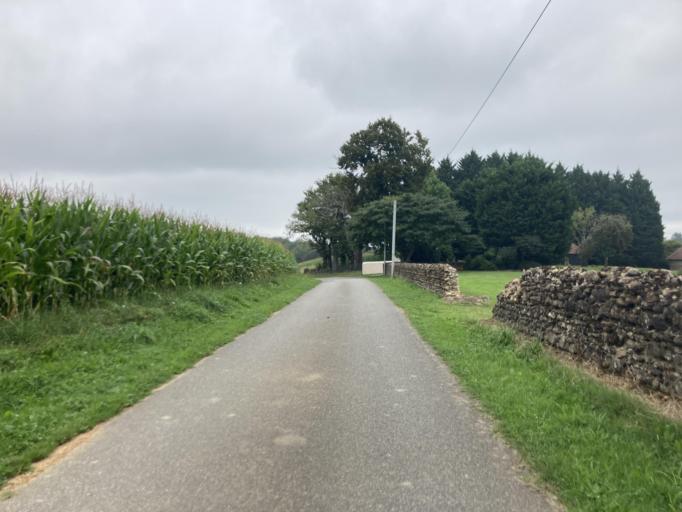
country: FR
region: Aquitaine
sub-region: Departement des Pyrenees-Atlantiques
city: Ledeuix
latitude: 43.2565
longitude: -0.6253
